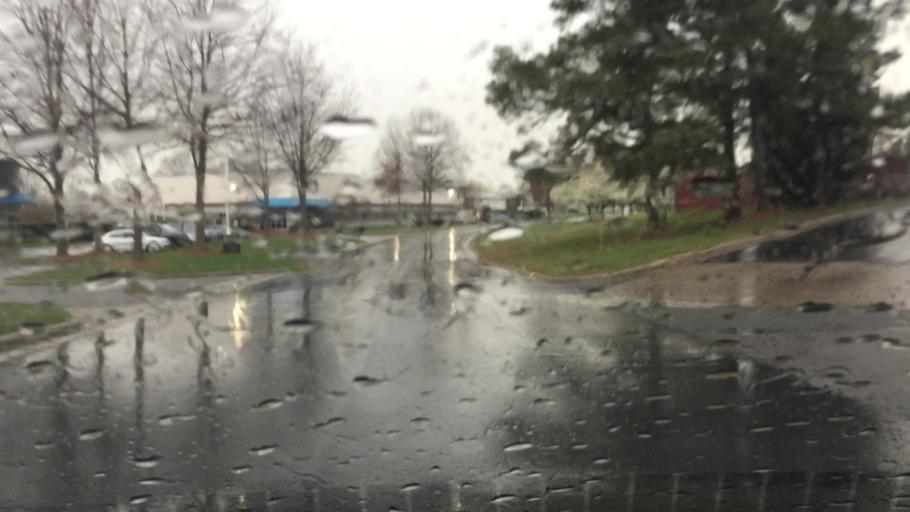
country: US
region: North Carolina
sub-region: Iredell County
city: Mooresville
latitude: 35.5907
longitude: -80.8658
